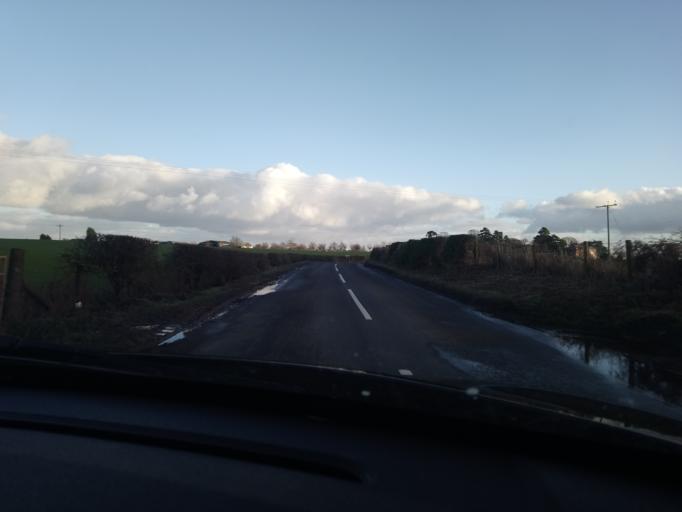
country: GB
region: England
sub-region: Shropshire
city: Petton
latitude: 52.8877
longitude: -2.7904
